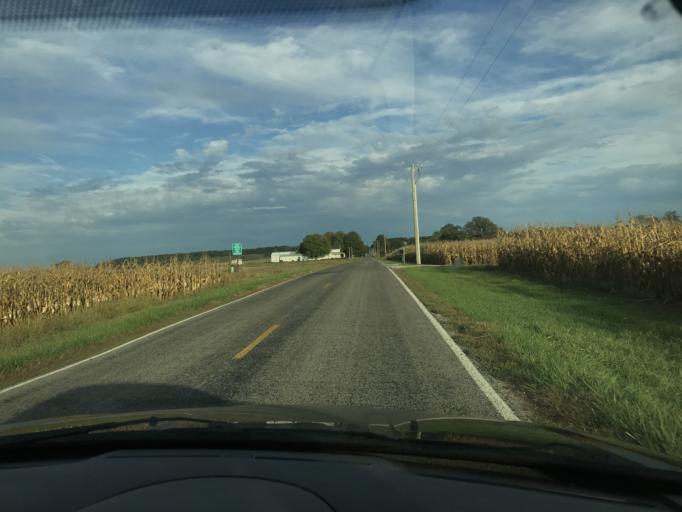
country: US
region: Ohio
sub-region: Logan County
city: West Liberty
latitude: 40.1943
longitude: -83.7913
